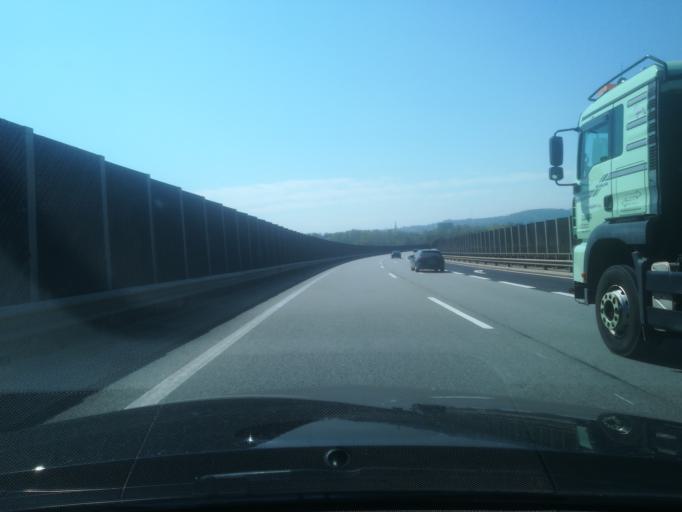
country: AT
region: Upper Austria
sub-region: Linz Stadt
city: Linz
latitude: 48.3300
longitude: 14.3249
